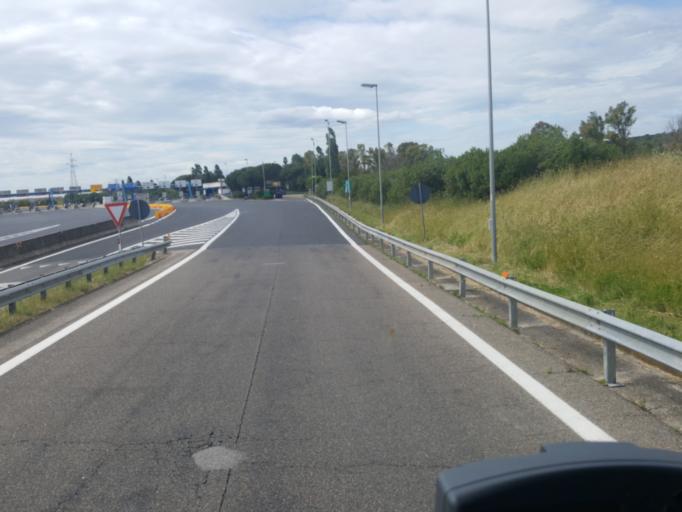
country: IT
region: Latium
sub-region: Citta metropolitana di Roma Capitale
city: Ara Nova
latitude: 41.9143
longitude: 12.2134
